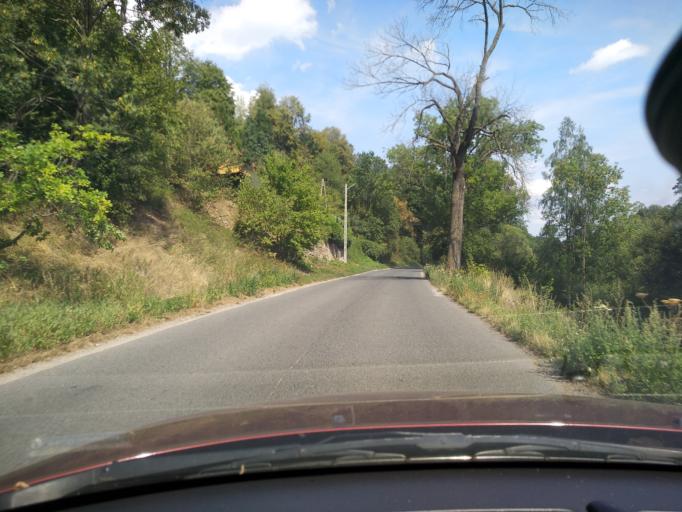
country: PL
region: Lower Silesian Voivodeship
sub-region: Powiat jeleniogorski
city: Stara Kamienica
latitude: 50.9346
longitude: 15.5836
